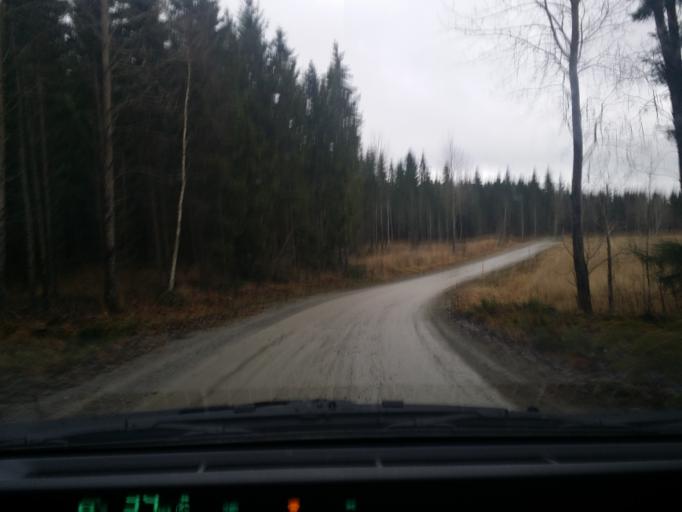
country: SE
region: Vaestmanland
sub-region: Vasteras
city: Skultuna
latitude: 59.7756
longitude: 16.3380
